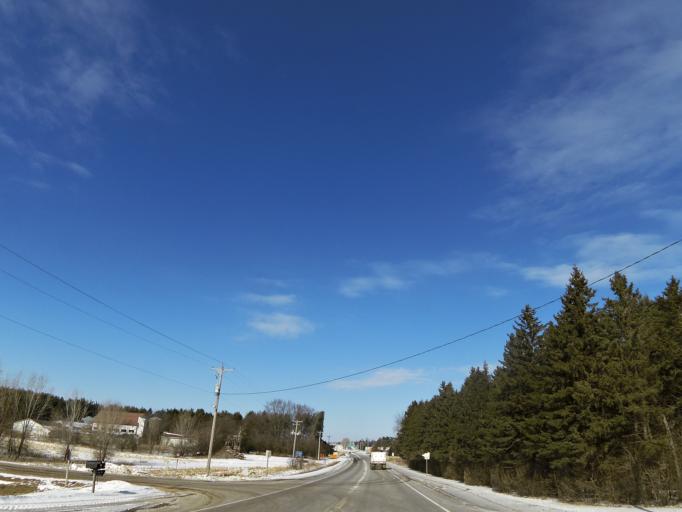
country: US
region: Wisconsin
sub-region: Saint Croix County
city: Roberts
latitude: 44.9865
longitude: -92.5581
